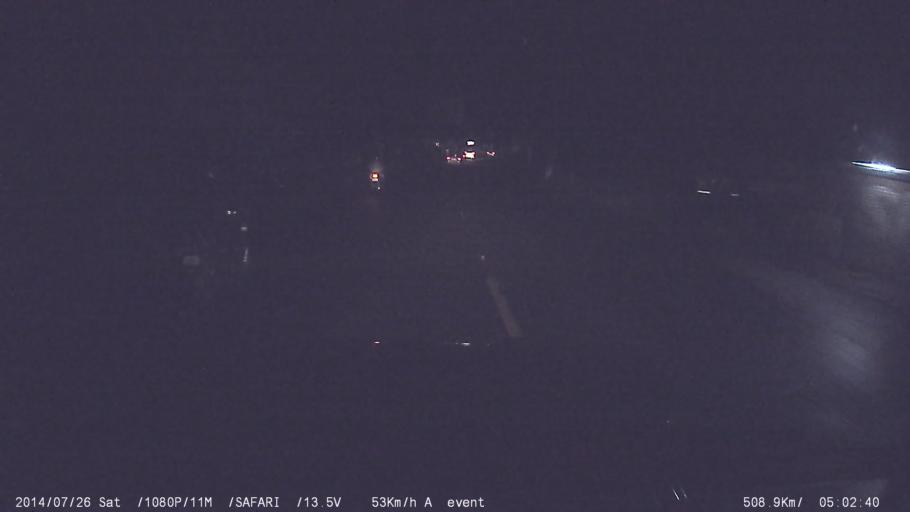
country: IN
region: Kerala
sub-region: Ernakulam
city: Perumbavoor
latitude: 10.1044
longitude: 76.4834
